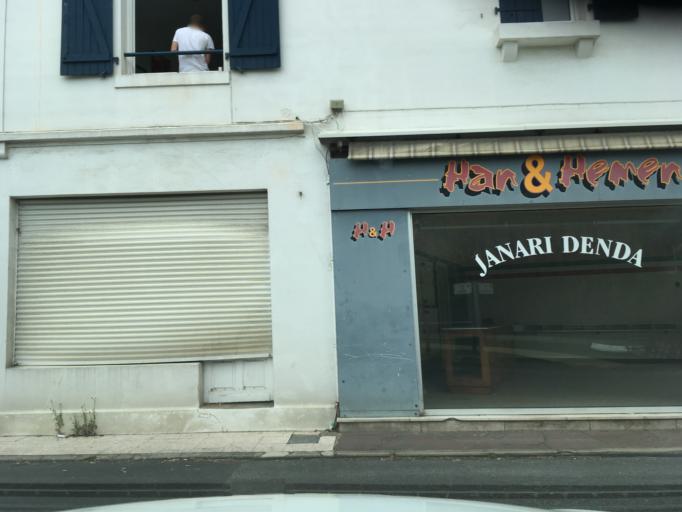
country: FR
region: Aquitaine
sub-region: Departement des Pyrenees-Atlantiques
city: Biarritz
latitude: 43.4786
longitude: -1.5349
